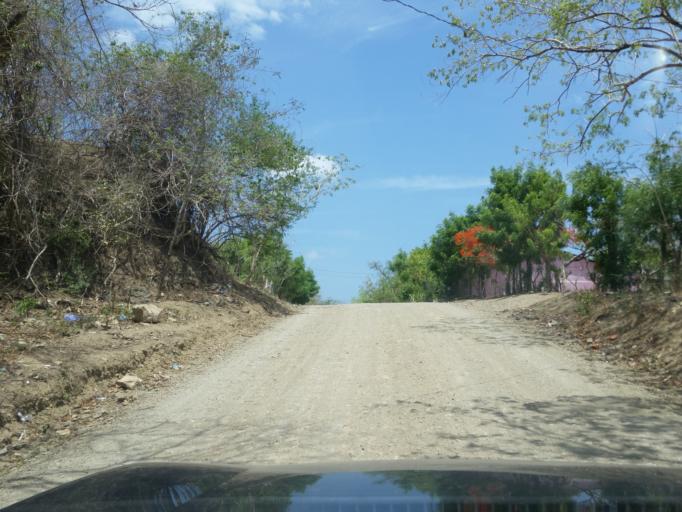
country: NI
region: Rivas
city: Tola
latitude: 11.5011
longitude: -86.0887
